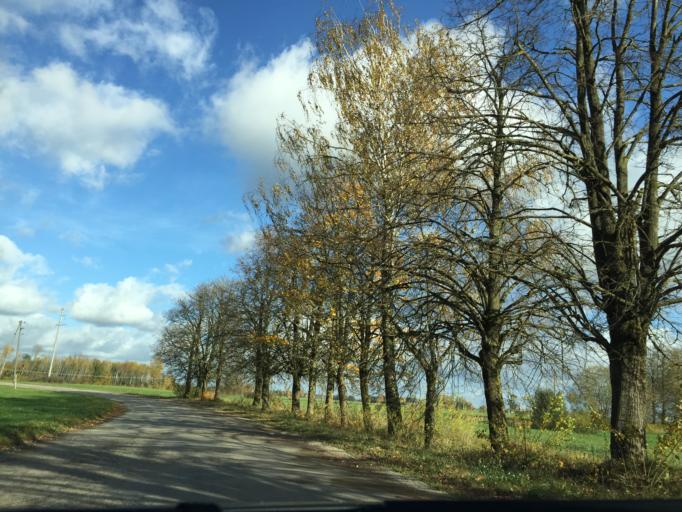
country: LV
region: Lielvarde
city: Lielvarde
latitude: 56.7175
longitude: 24.8646
